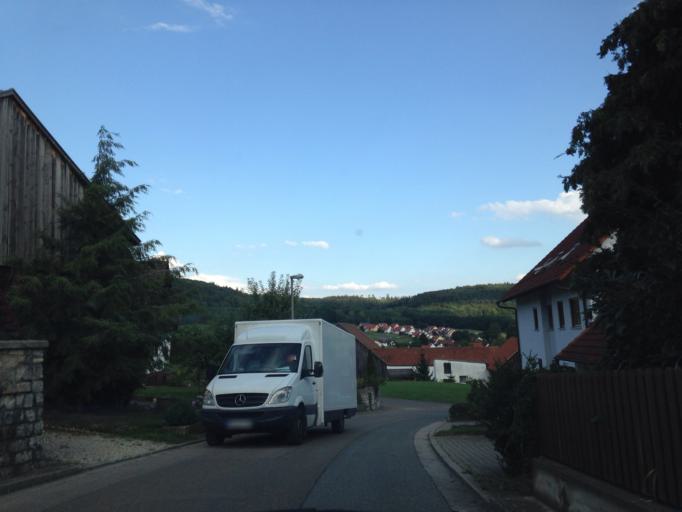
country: DE
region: Bavaria
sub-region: Regierungsbezirk Mittelfranken
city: Greding
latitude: 49.1142
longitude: 11.3057
